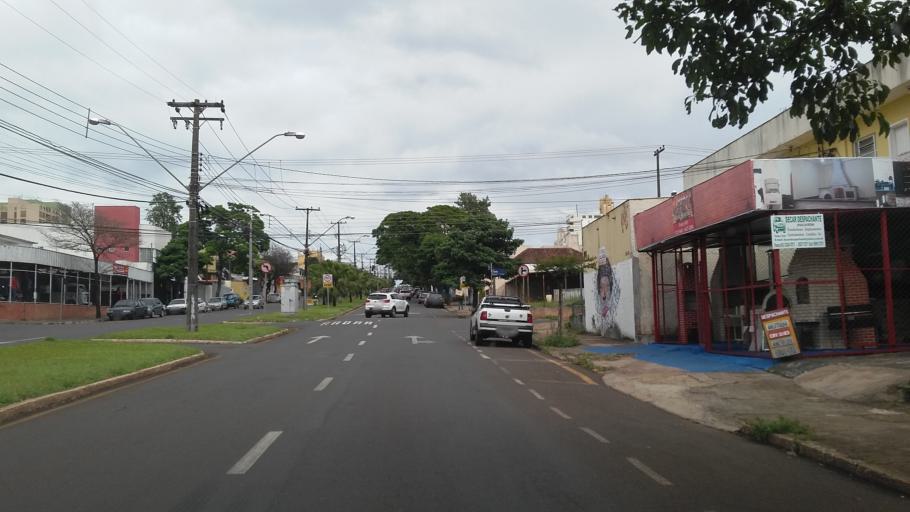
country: BR
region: Parana
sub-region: Londrina
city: Londrina
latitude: -23.3198
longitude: -51.1508
